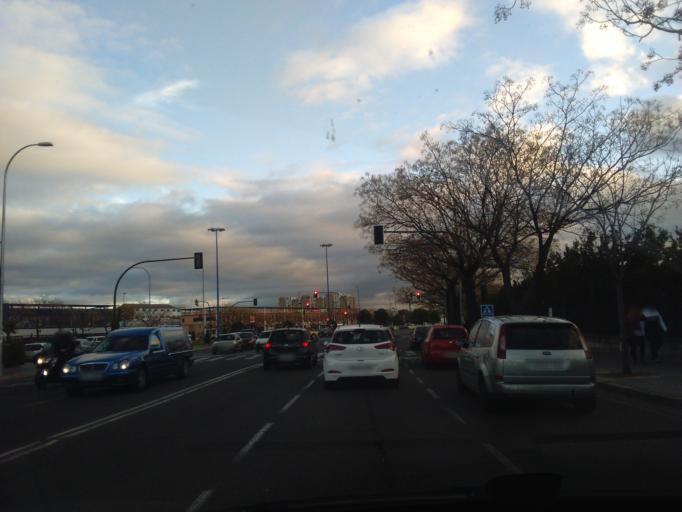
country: ES
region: Andalusia
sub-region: Provincia de Sevilla
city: Sevilla
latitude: 37.3911
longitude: -5.9596
